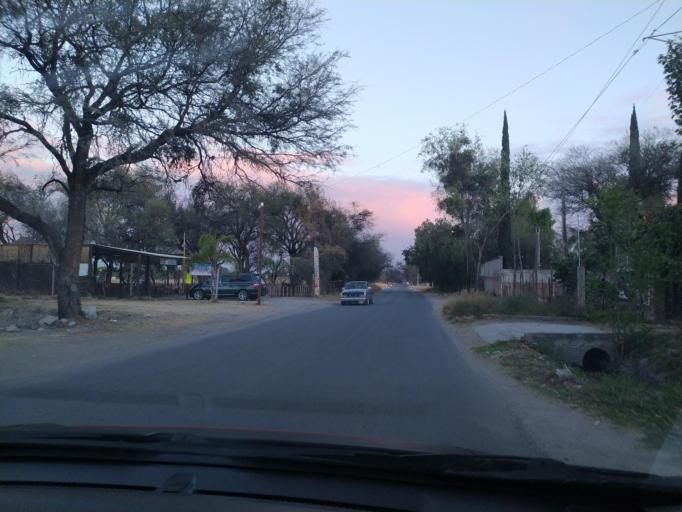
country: MX
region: Guanajuato
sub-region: San Francisco del Rincon
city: Fraccionamiento la Mezquitera
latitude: 21.0205
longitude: -101.8256
